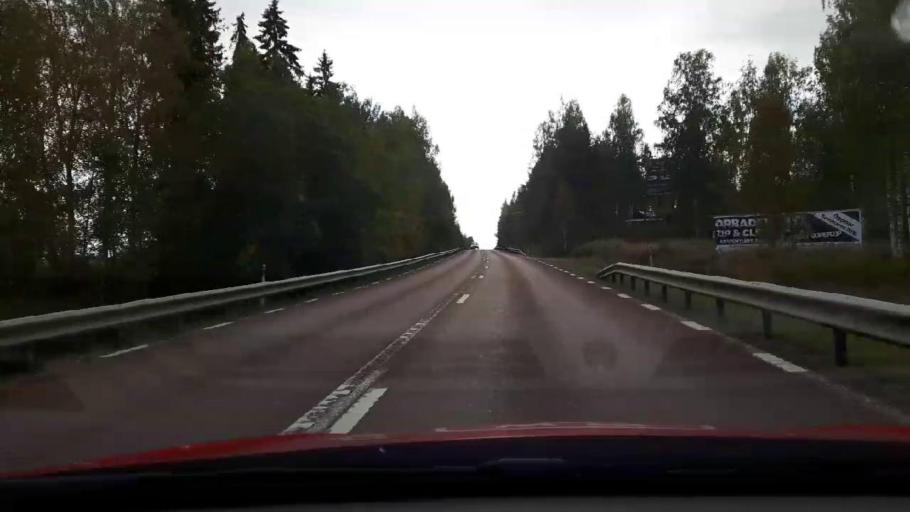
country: SE
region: Gaevleborg
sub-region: Bollnas Kommun
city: Arbra
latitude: 61.5510
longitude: 16.3496
